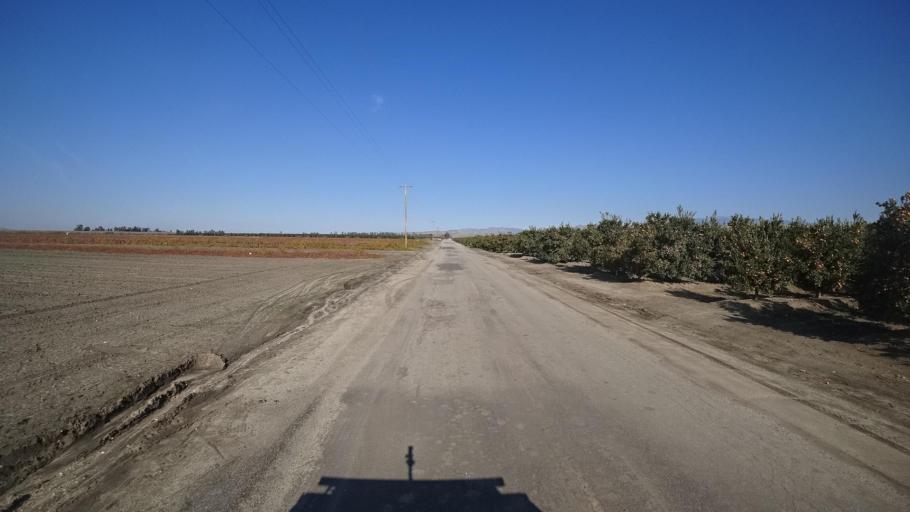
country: US
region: California
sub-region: Kern County
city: Arvin
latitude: 35.2849
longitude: -118.7708
